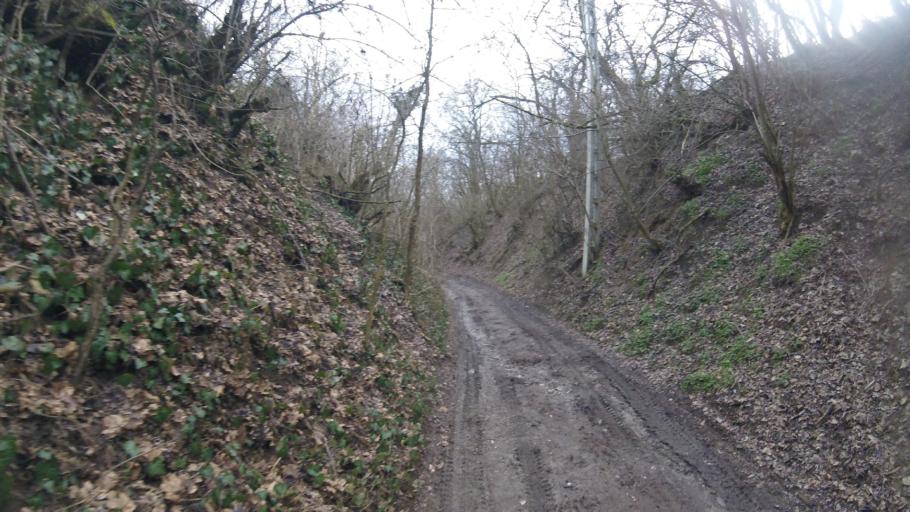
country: HU
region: Pest
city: Nagykovacsi
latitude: 47.6663
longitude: 19.0135
